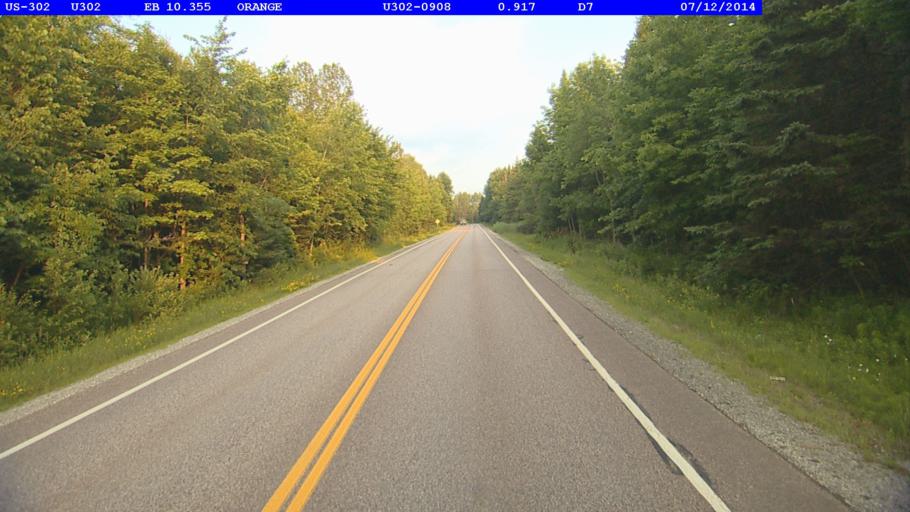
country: US
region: Vermont
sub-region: Washington County
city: South Barre
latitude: 44.1522
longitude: -72.4197
